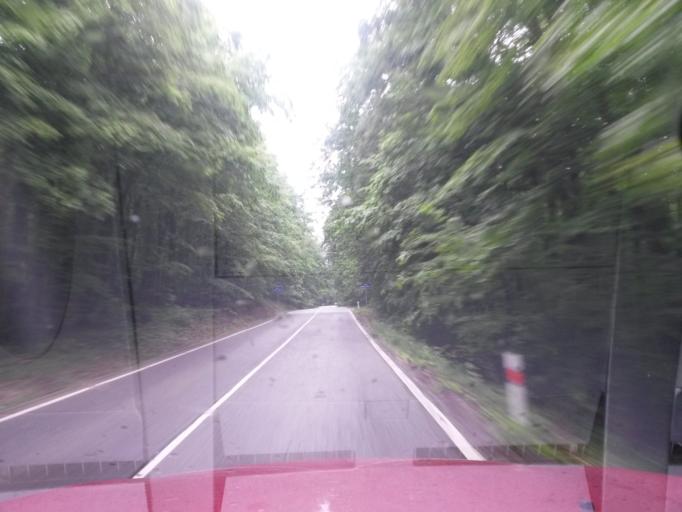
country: SK
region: Kosicky
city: Kosice
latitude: 48.7137
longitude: 21.1905
